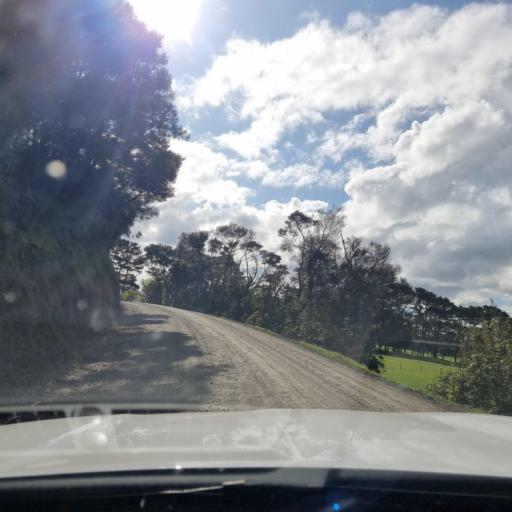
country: NZ
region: Auckland
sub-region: Auckland
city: Wellsford
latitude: -36.3155
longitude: 174.1344
